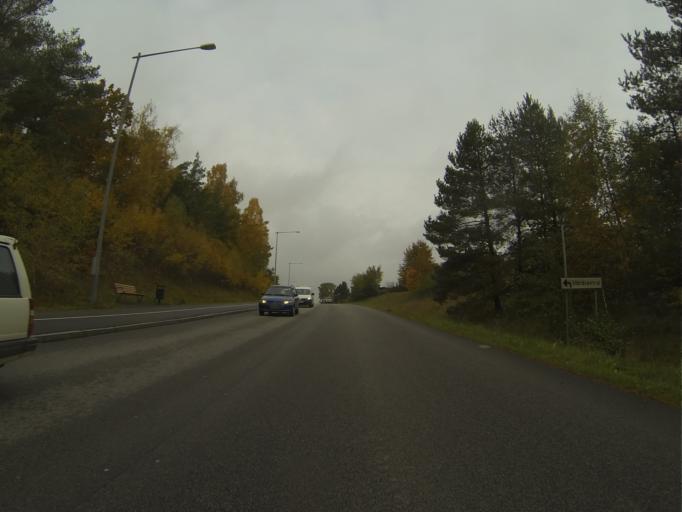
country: SE
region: Skane
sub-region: Sjobo Kommun
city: Sjoebo
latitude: 55.6255
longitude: 13.7050
